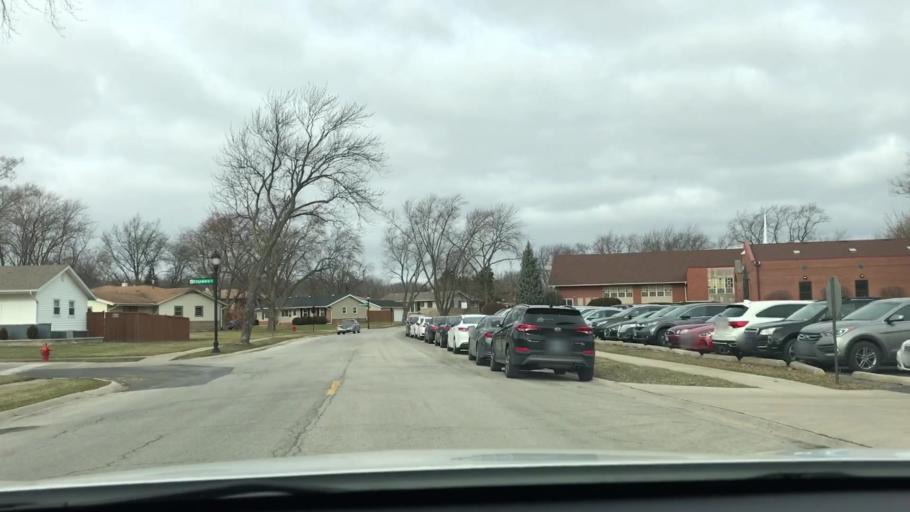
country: US
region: Illinois
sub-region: Cook County
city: Elk Grove Village
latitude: 42.0157
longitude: -87.9896
